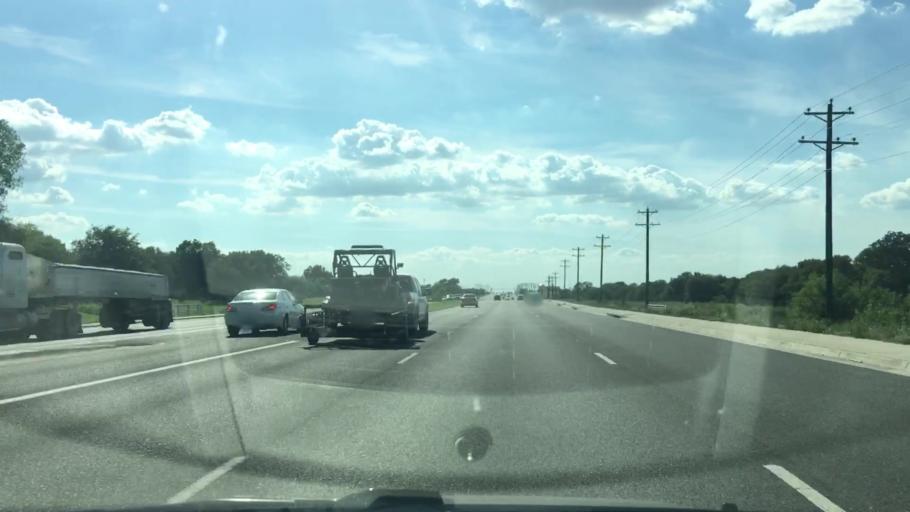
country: US
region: Texas
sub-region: Collin County
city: Prosper
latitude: 33.2186
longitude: -96.7512
